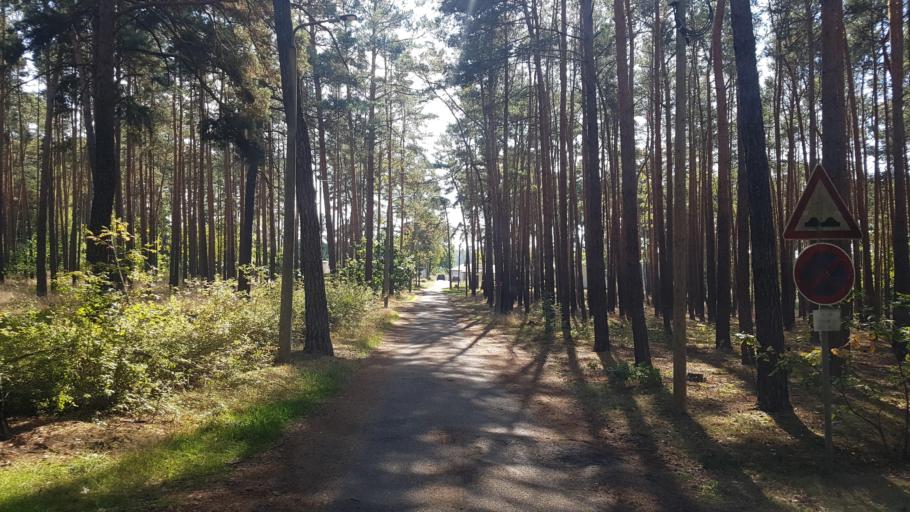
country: DE
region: Brandenburg
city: Lebusa
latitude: 51.8188
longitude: 13.4023
